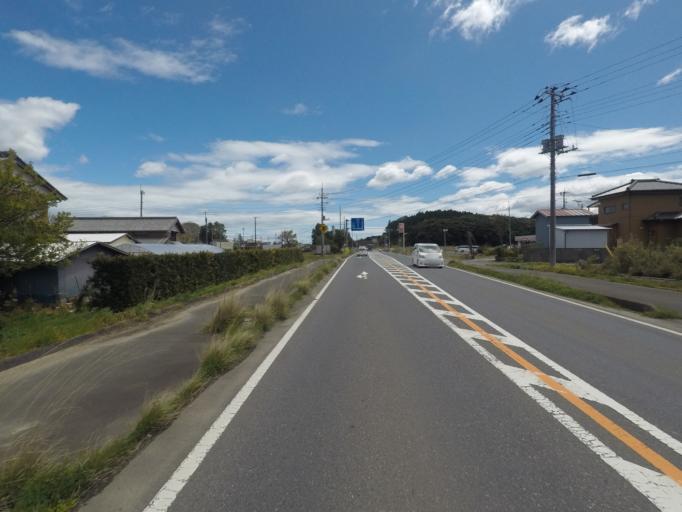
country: JP
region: Ibaraki
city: Itako
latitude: 36.0935
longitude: 140.5154
